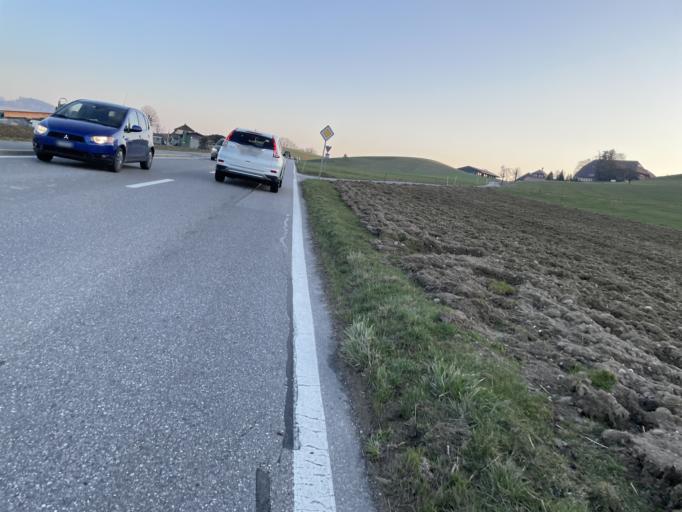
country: CH
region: Bern
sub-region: Bern-Mittelland District
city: Worb
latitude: 46.9216
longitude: 7.5667
